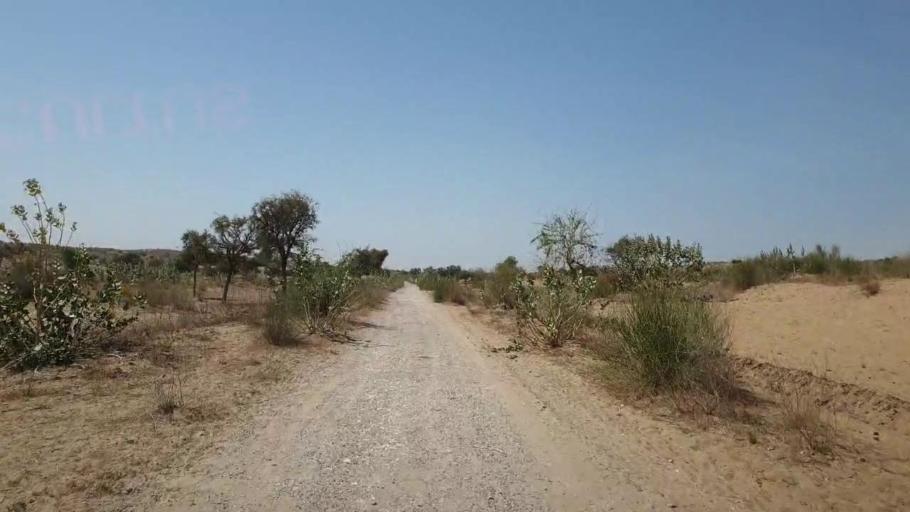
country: PK
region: Sindh
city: Umarkot
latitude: 25.1534
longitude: 69.9449
